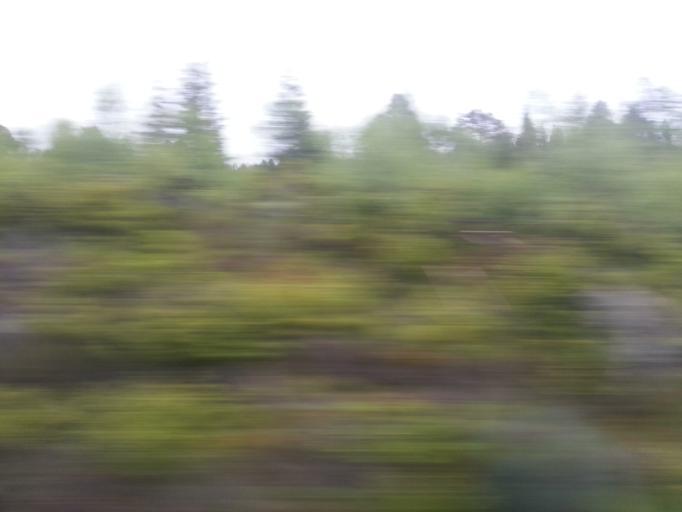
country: NO
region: Sor-Trondelag
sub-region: Rennebu
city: Berkak
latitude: 62.8317
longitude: 10.0196
